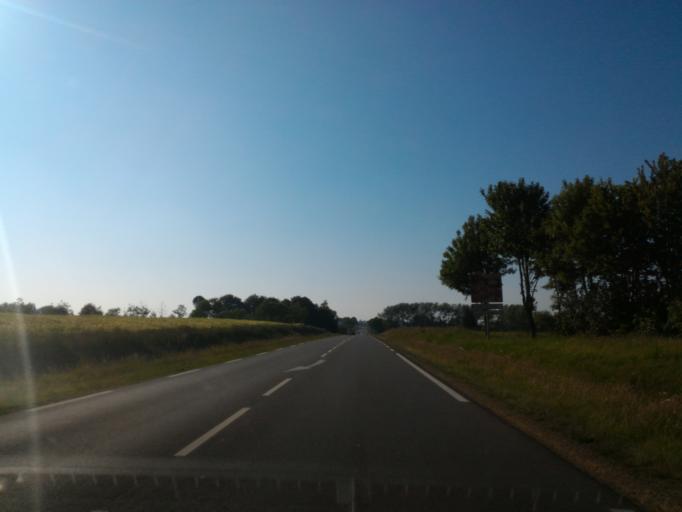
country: FR
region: Brittany
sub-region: Departement d'Ille-et-Vilaine
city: Saint-Germain-en-Cogles
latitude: 48.3905
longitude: -1.2817
